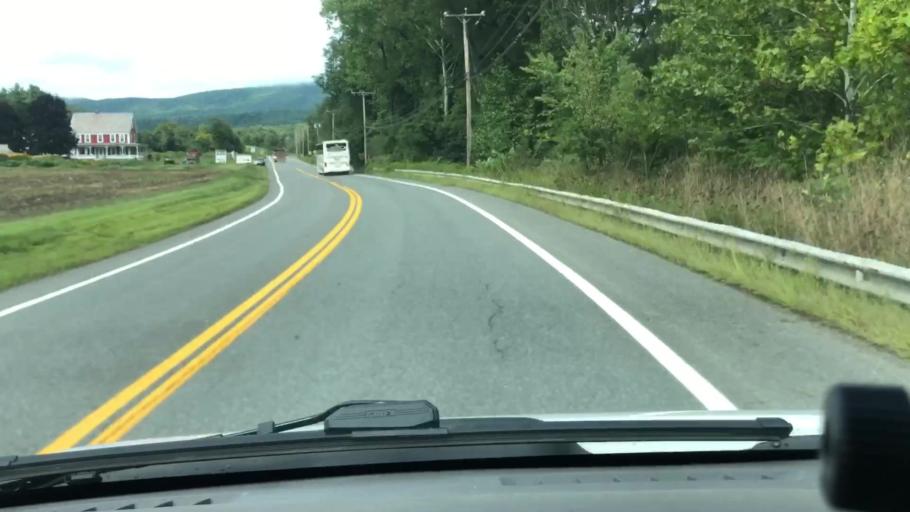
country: US
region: Massachusetts
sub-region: Franklin County
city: Buckland
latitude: 42.6049
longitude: -72.7749
